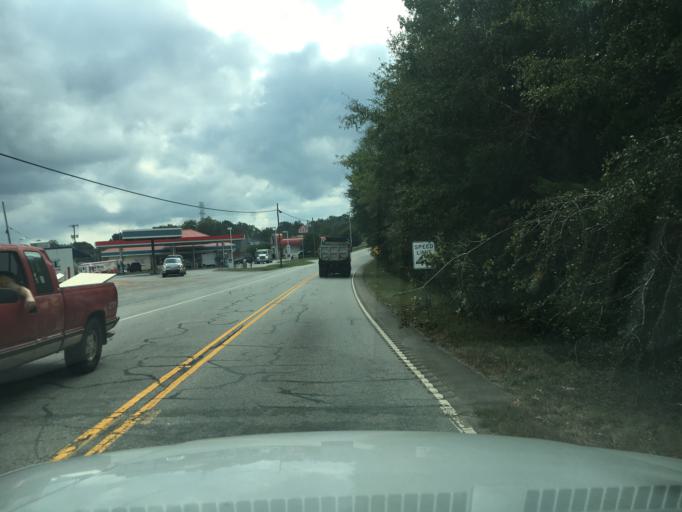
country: US
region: South Carolina
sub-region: Greenville County
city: Greer
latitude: 34.9924
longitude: -82.2455
